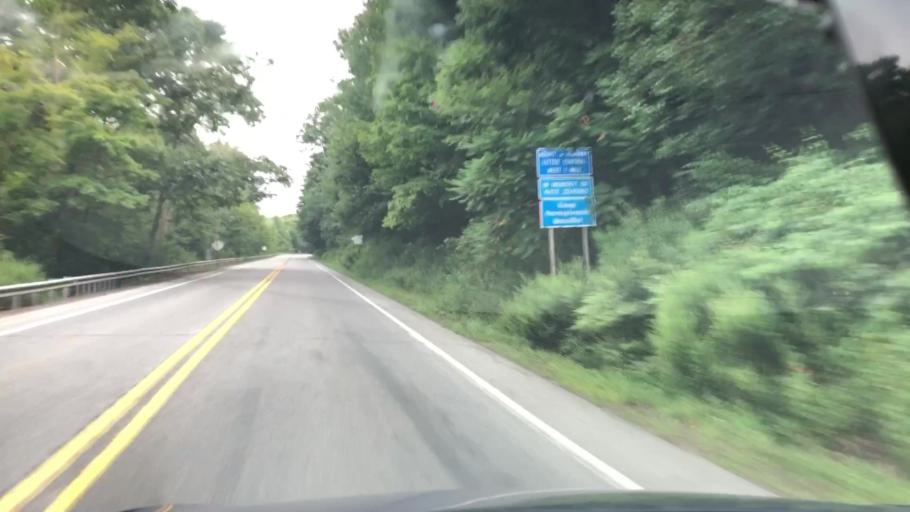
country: US
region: Pennsylvania
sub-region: Crawford County
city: Titusville
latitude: 41.6170
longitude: -79.6717
